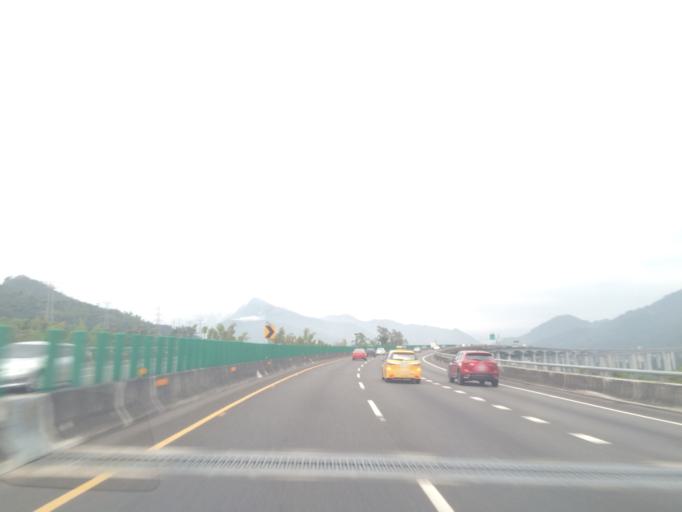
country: TW
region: Taiwan
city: Zhongxing New Village
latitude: 23.9969
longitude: 120.8018
